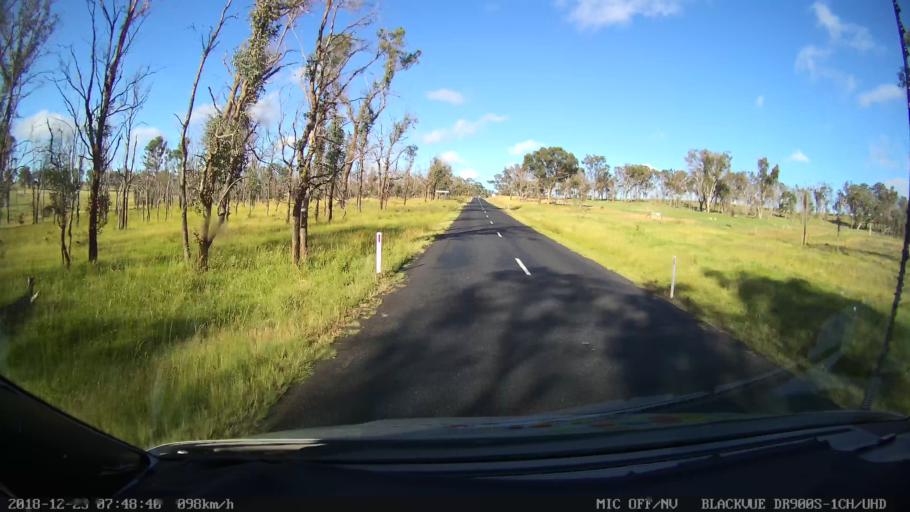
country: AU
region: New South Wales
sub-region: Armidale Dumaresq
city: Armidale
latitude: -30.5334
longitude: 151.8821
